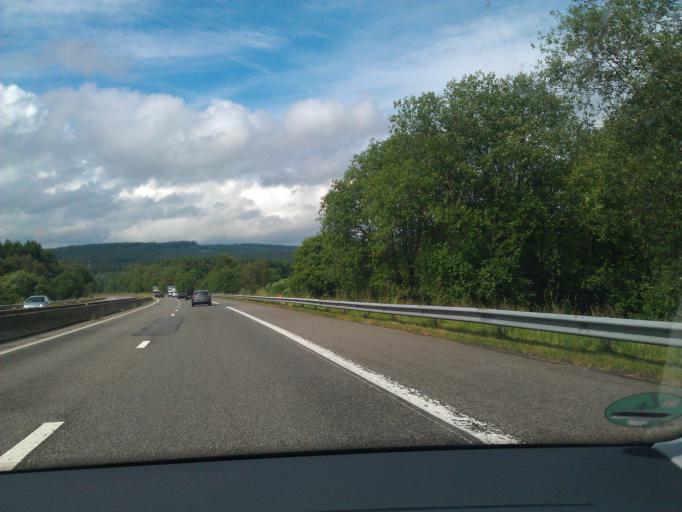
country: BE
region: Wallonia
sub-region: Province de Liege
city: Saint-Vith
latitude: 50.3290
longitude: 6.0907
